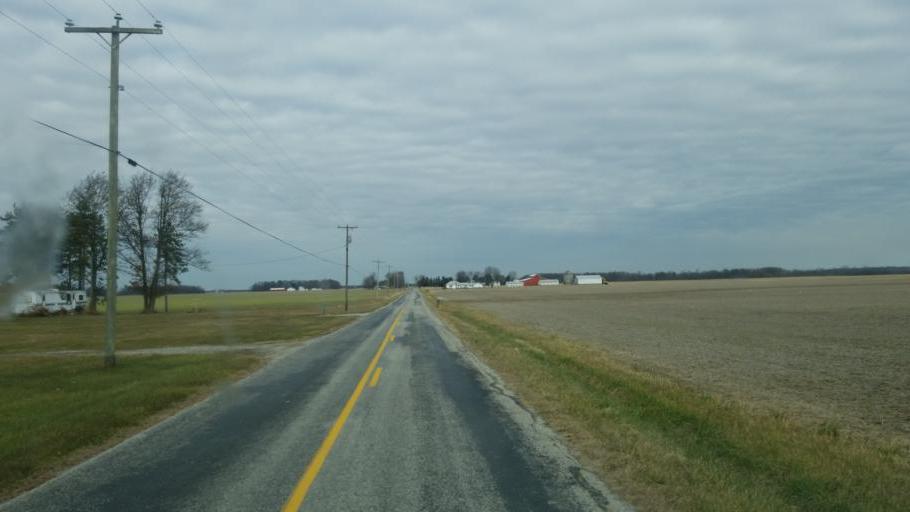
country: US
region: Ohio
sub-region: Hardin County
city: Forest
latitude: 40.6548
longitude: -83.4196
